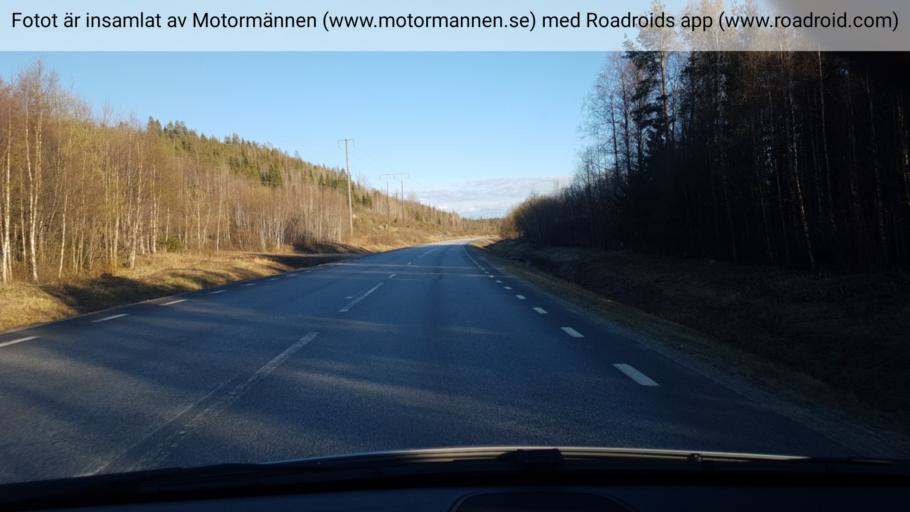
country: SE
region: Vaesterbotten
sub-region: Vannas Kommun
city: Vaennaes
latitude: 63.9942
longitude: 19.7301
